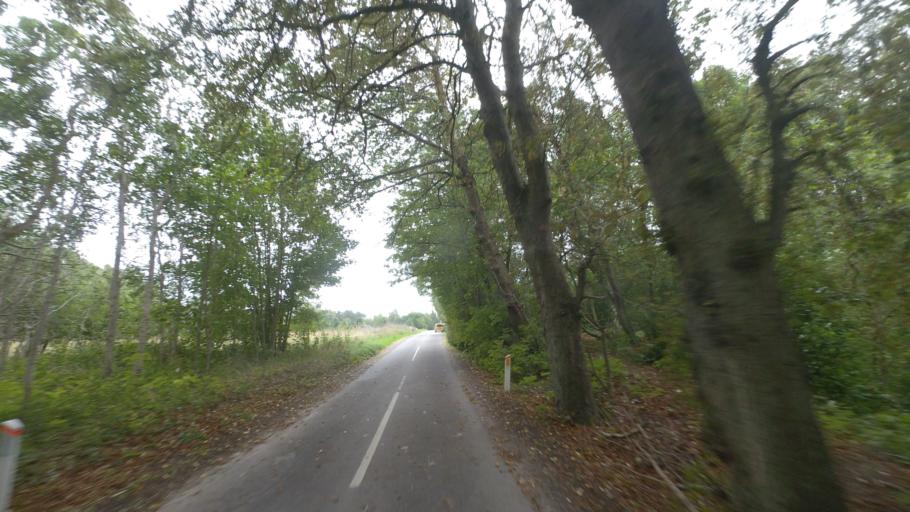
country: DK
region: Capital Region
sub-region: Bornholm Kommune
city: Akirkeby
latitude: 55.0049
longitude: 14.9926
